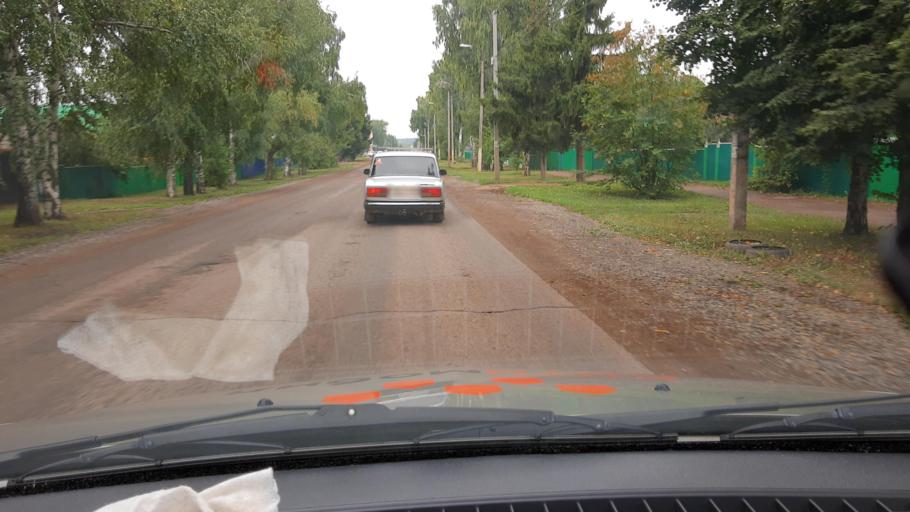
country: RU
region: Bashkortostan
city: Buzdyak
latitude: 54.5695
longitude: 54.5299
